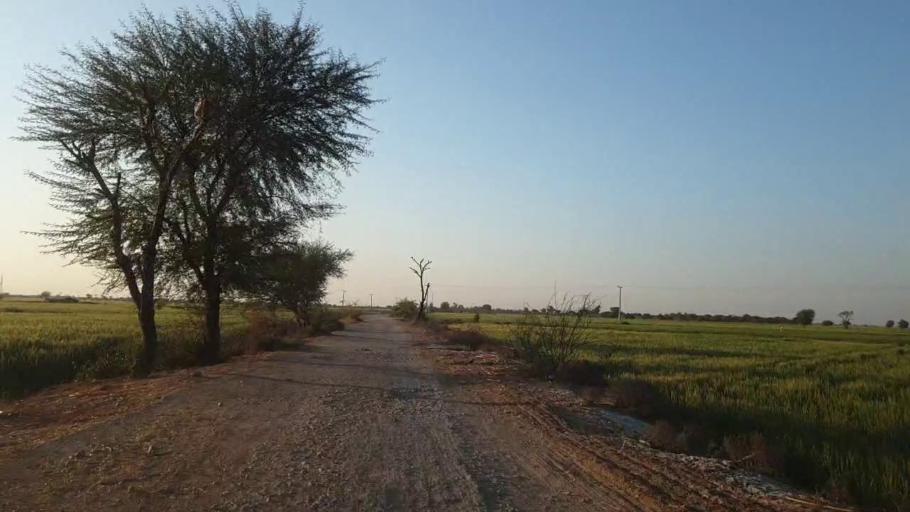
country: PK
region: Sindh
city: Mirpur Khas
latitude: 25.6958
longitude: 69.0489
